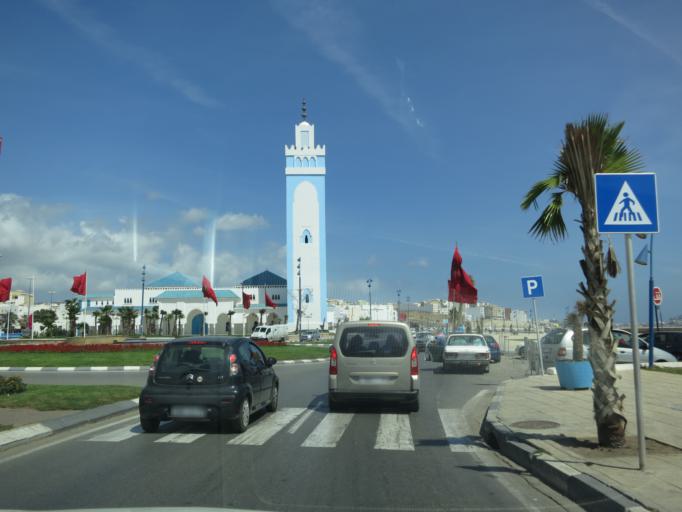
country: ES
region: Ceuta
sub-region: Ceuta
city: Ceuta
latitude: 35.8457
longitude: -5.3540
